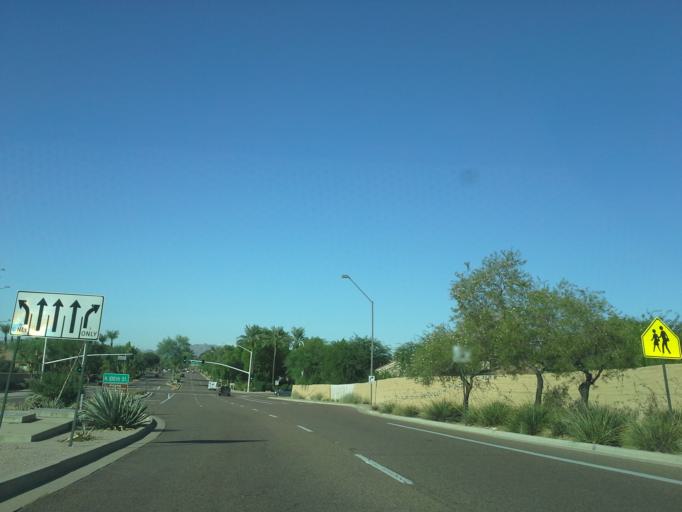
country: US
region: Arizona
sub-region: Maricopa County
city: Paradise Valley
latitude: 33.6249
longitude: -111.8707
